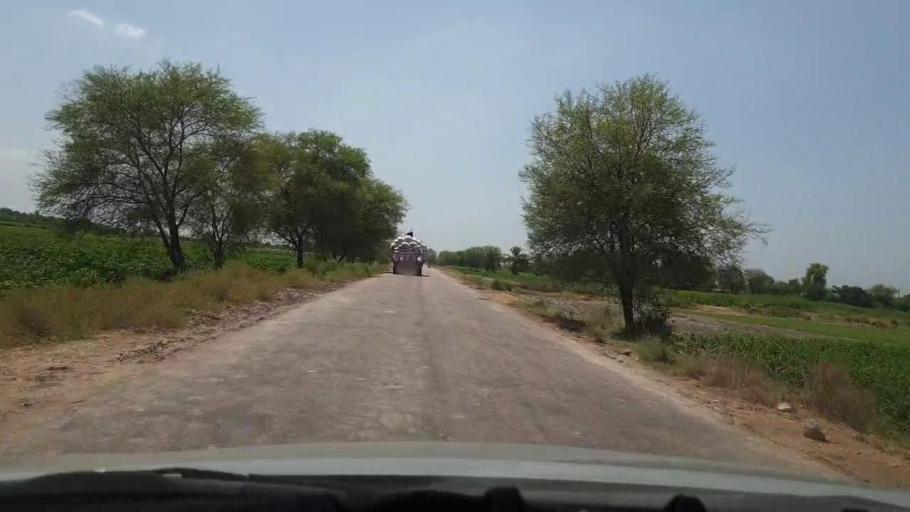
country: PK
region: Sindh
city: Pano Aqil
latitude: 27.6634
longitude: 69.1483
